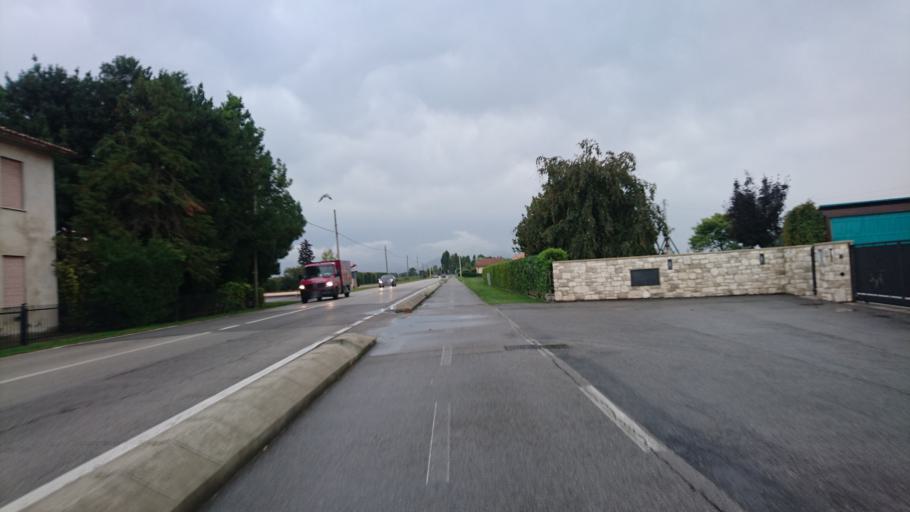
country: IT
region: Veneto
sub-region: Provincia di Vicenza
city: Grisignano di Zocco
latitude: 45.4712
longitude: 11.6977
